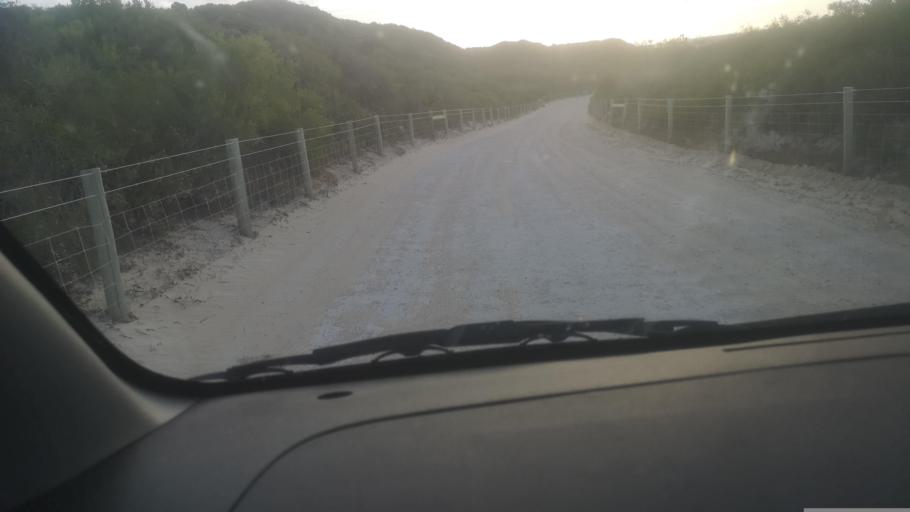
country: AU
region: Western Australia
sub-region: Wanneroo
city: Two Rocks
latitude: -31.5197
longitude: 115.6088
